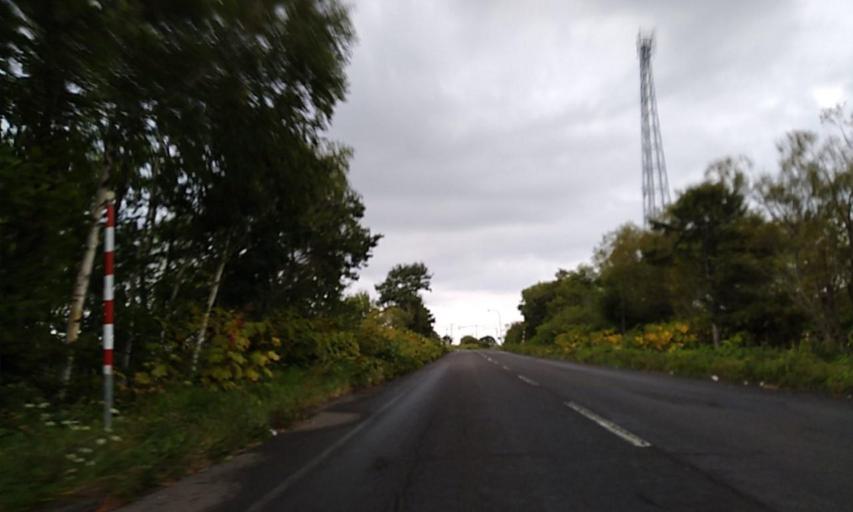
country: JP
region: Hokkaido
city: Mombetsu
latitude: 44.6197
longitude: 142.9205
